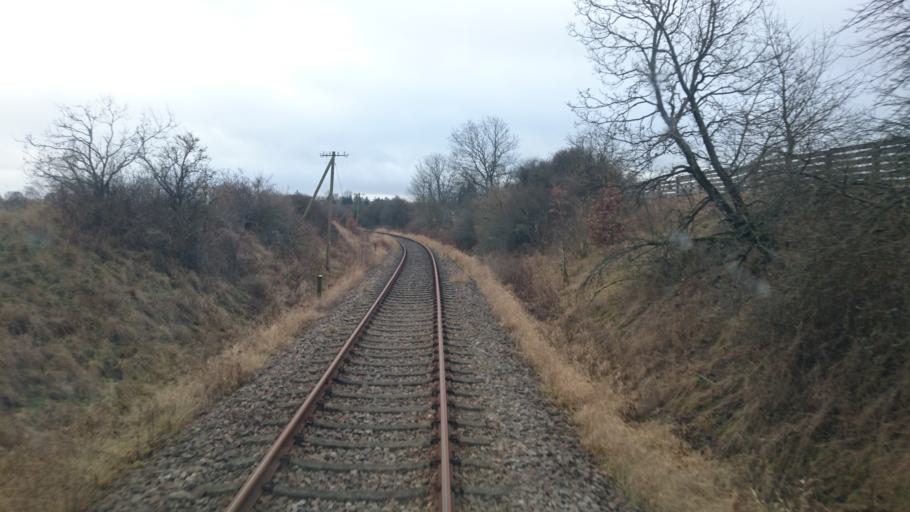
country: DE
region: Saxony
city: Muhltroff
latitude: 50.5450
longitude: 11.9197
